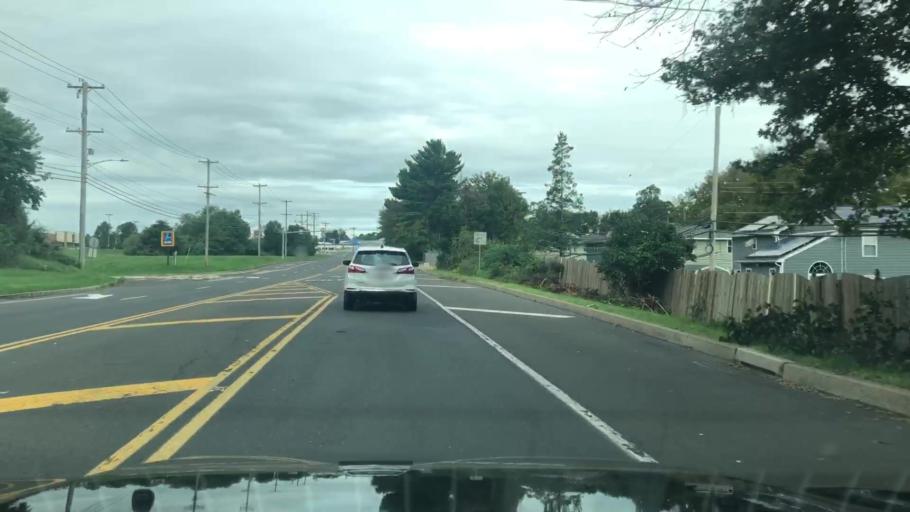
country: US
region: Pennsylvania
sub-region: Bucks County
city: Woodbourne
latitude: 40.1717
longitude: -74.8811
